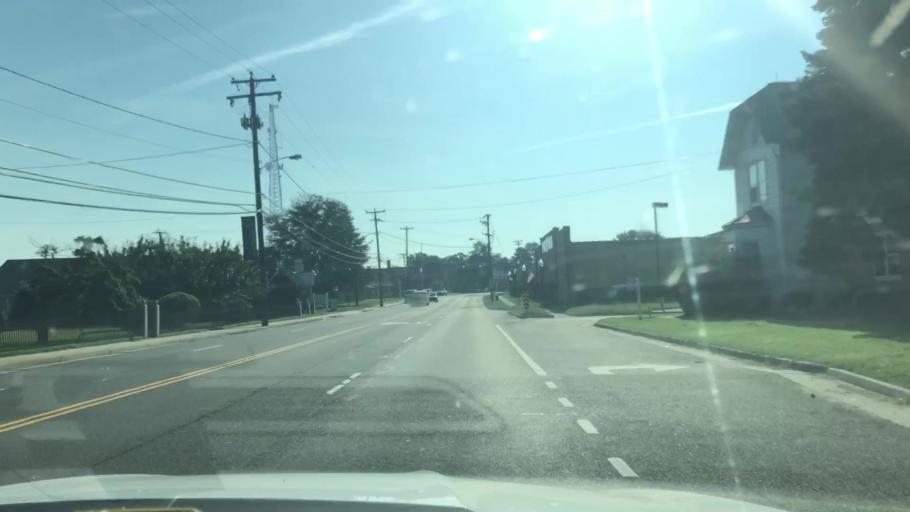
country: US
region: Virginia
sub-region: Richmond County
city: Warsaw
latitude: 37.9586
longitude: -76.7613
